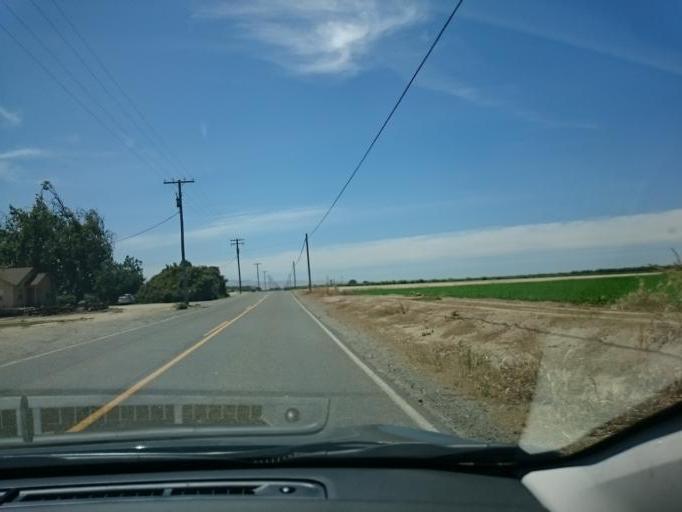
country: US
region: California
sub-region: Stanislaus County
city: Bret Harte
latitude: 37.5515
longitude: -121.0181
